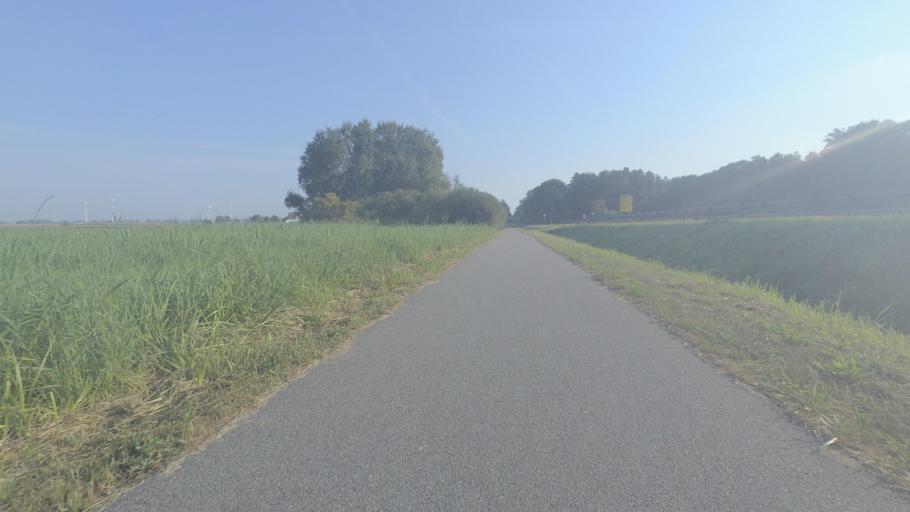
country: DE
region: Mecklenburg-Vorpommern
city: Tutow
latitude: 53.9831
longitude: 13.1502
